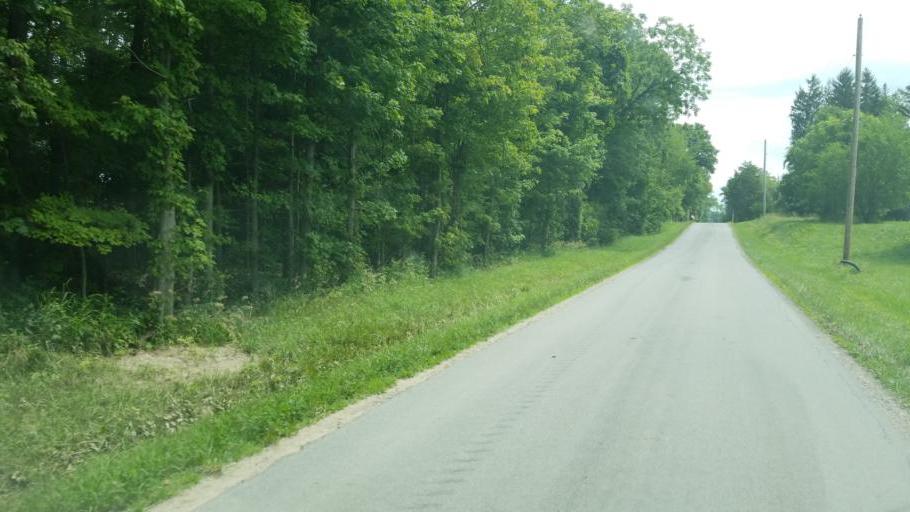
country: US
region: Ohio
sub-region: Wyandot County
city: Upper Sandusky
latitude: 40.8770
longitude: -83.1469
